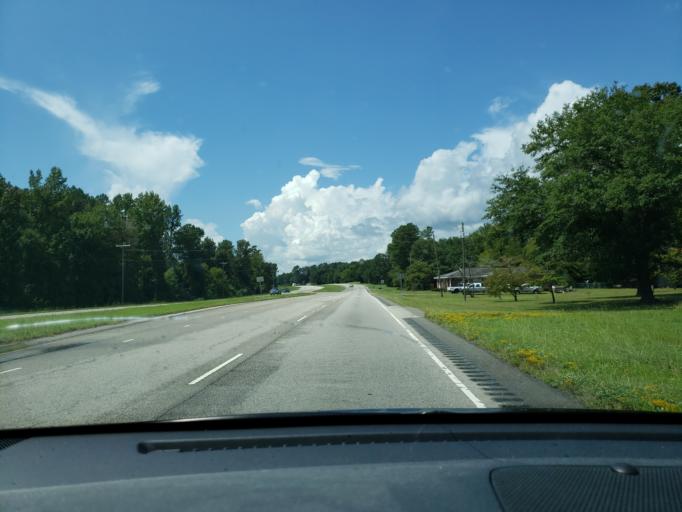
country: US
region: North Carolina
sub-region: Bladen County
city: Elizabethtown
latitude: 34.6448
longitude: -78.6851
